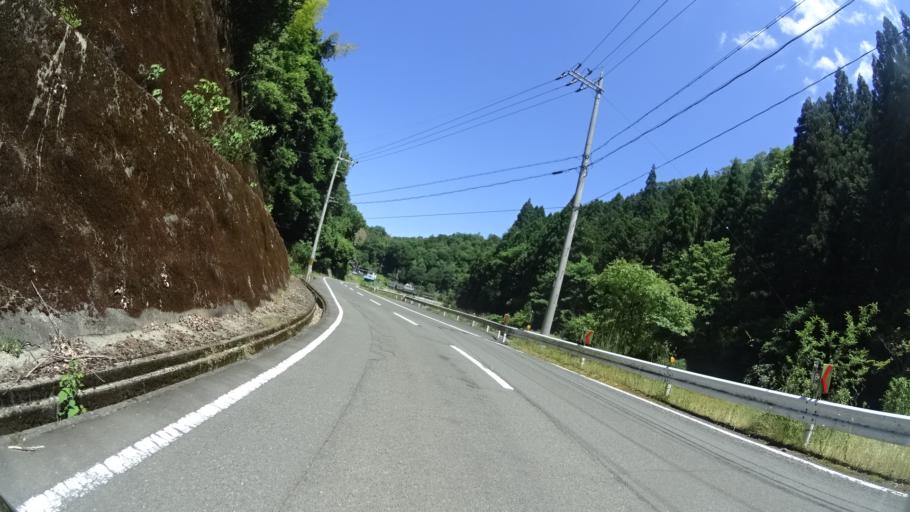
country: JP
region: Kyoto
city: Miyazu
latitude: 35.4389
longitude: 135.1895
